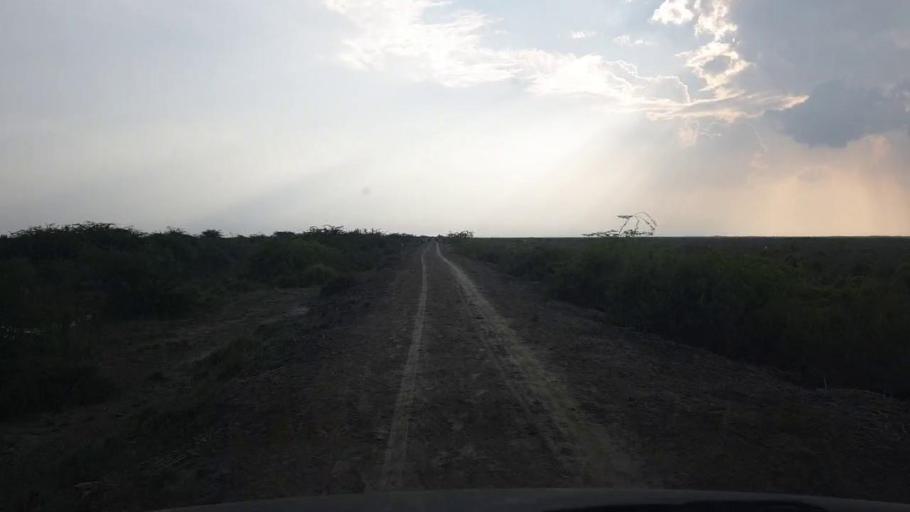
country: PK
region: Sindh
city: Badin
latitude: 24.4637
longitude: 68.6919
